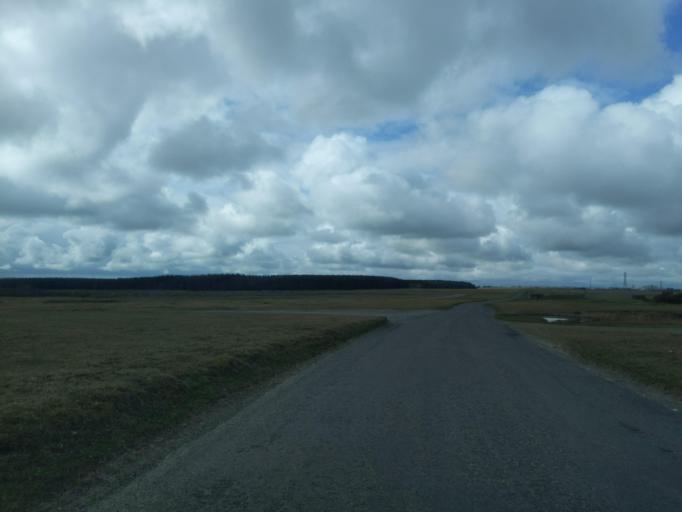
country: GB
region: England
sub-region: Cornwall
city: Camelford
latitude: 50.6307
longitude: -4.6053
